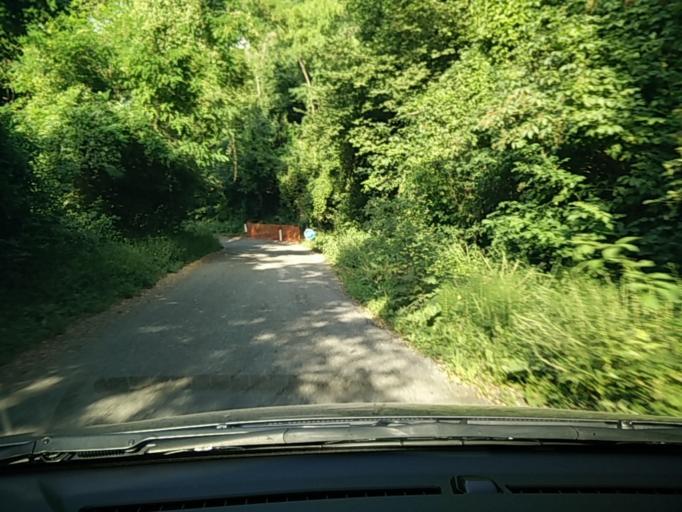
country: IT
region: Lombardy
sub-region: Provincia di Pavia
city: Susella
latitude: 44.9198
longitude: 9.1010
